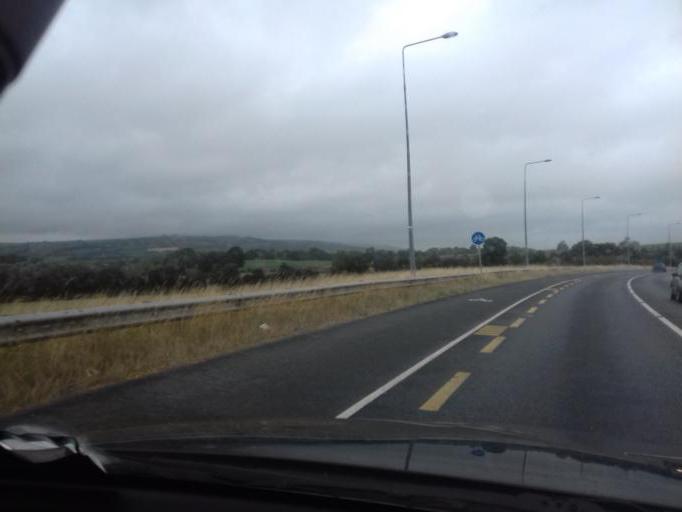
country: IE
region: Leinster
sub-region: County Carlow
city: Bagenalstown
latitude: 52.7642
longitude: -6.9560
